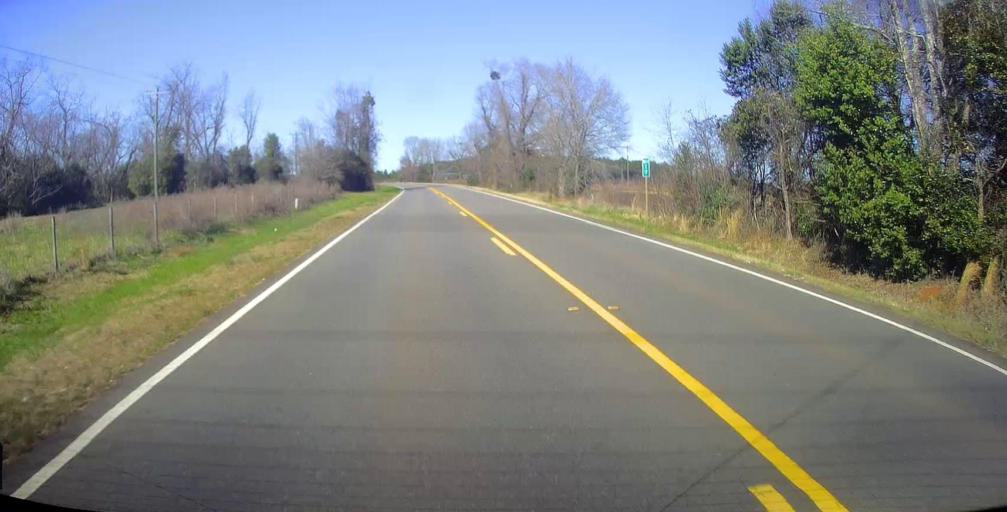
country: US
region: Georgia
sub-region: Macon County
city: Montezuma
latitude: 32.3868
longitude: -84.0156
